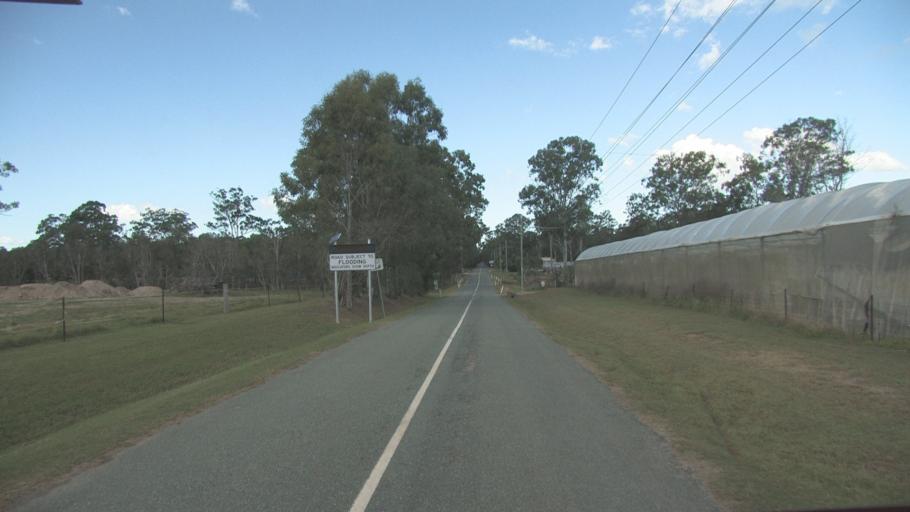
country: AU
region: Queensland
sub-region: Gold Coast
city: Yatala
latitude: -27.6668
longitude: 153.2335
